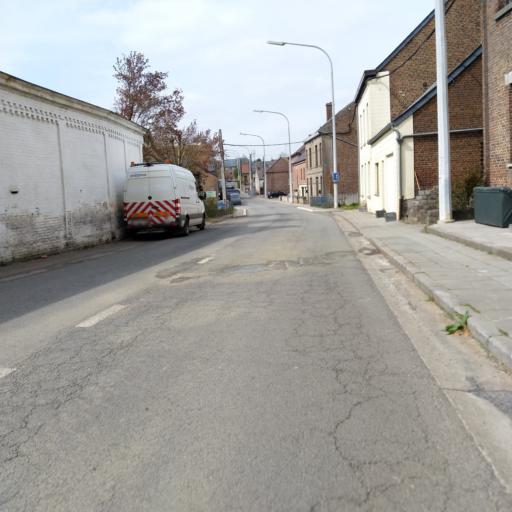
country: BE
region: Wallonia
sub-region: Province du Hainaut
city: Quevy-le-Petit
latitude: 50.3674
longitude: 3.9374
